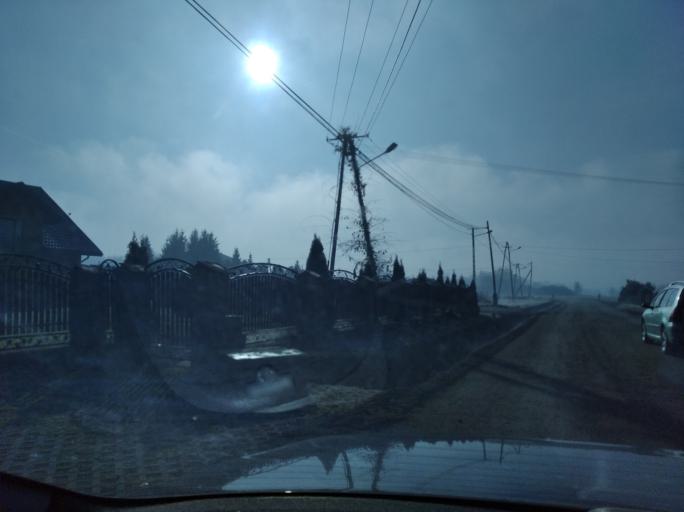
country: PL
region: Subcarpathian Voivodeship
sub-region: Powiat strzyzowski
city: Wisniowa
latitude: 49.8695
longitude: 21.7059
